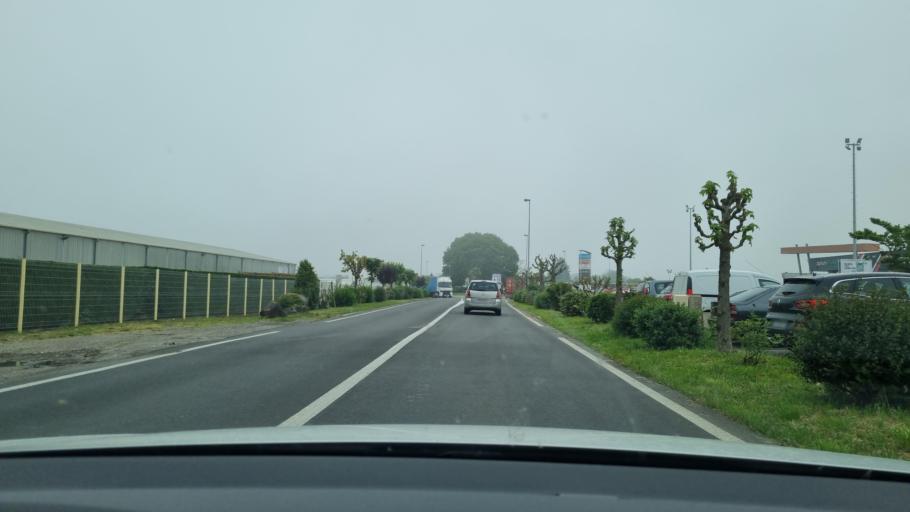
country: FR
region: Aquitaine
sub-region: Departement des Landes
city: Hagetmau
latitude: 43.6361
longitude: -0.6155
